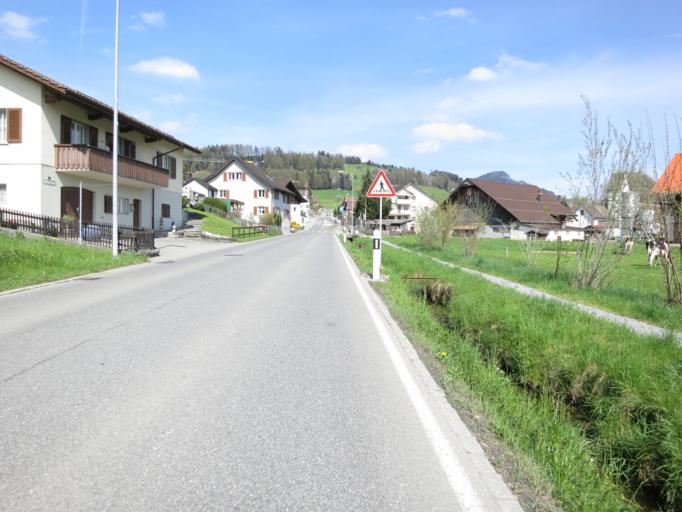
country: CH
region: Saint Gallen
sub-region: Wahlkreis See-Gaster
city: Schmerikon
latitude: 47.2480
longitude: 8.9433
